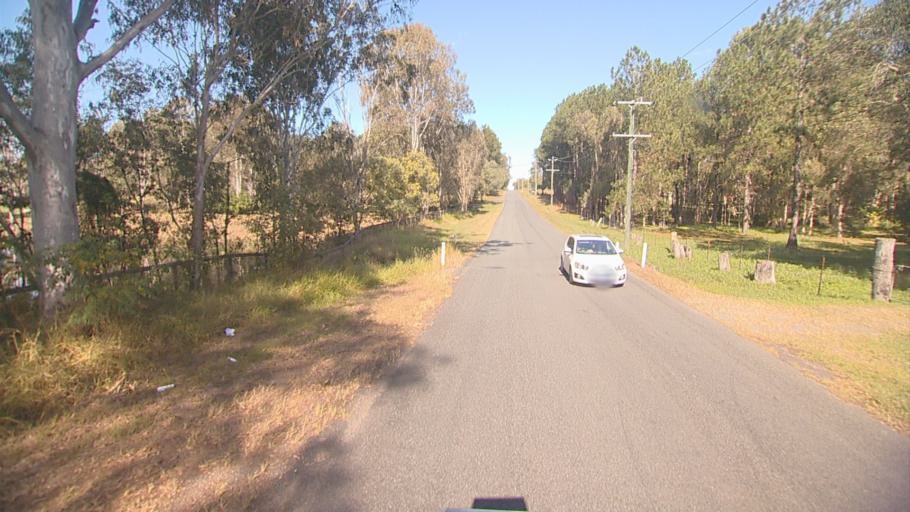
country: AU
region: Queensland
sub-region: Logan
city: North Maclean
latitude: -27.7745
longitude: 152.9915
